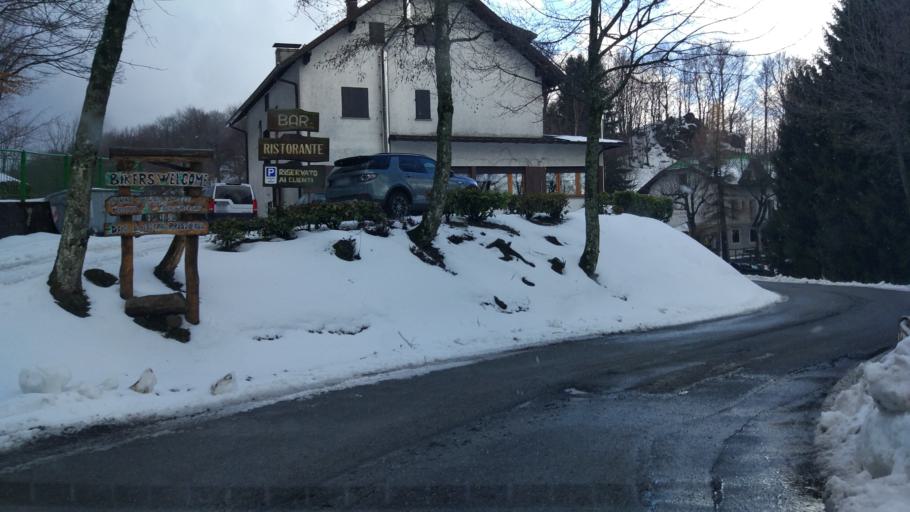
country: IT
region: Lombardy
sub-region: Provincia di Lecco
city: Morterone
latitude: 45.9027
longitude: 9.4947
